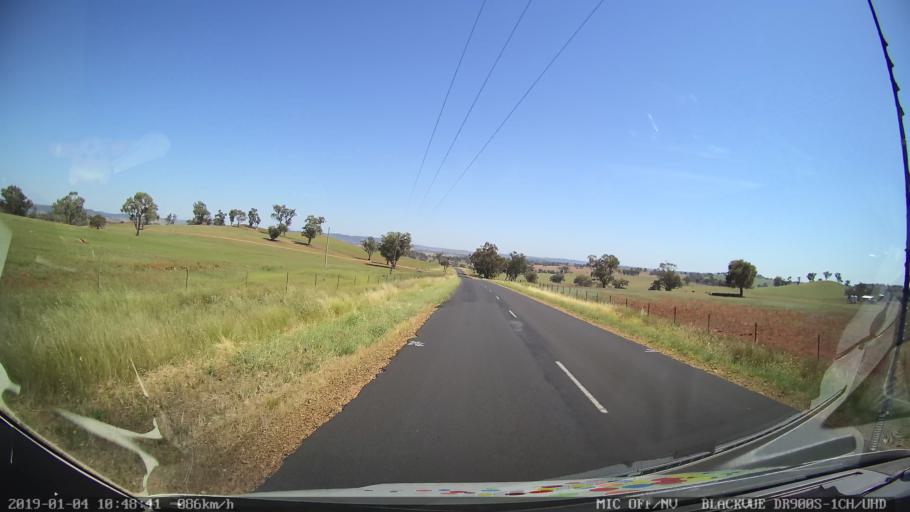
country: AU
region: New South Wales
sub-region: Cabonne
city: Molong
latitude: -33.2568
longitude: 148.7119
